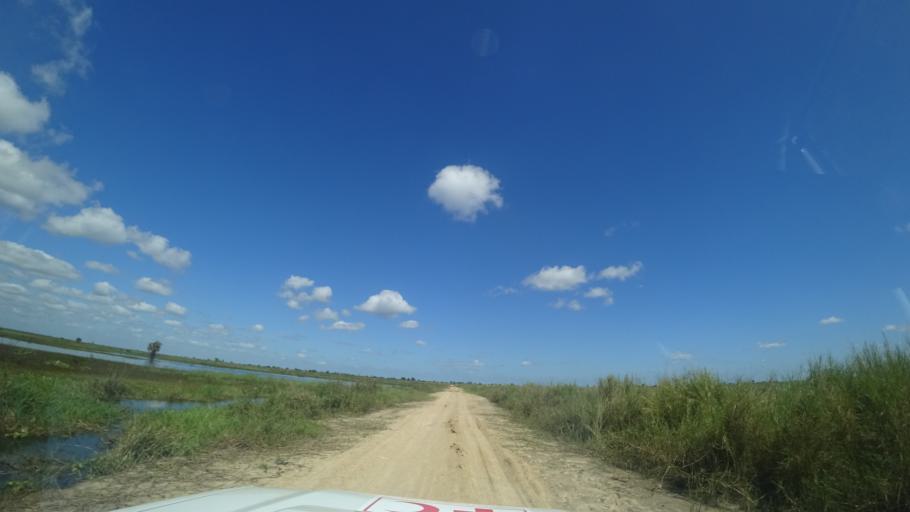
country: MZ
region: Sofala
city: Dondo
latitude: -19.3942
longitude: 34.5739
